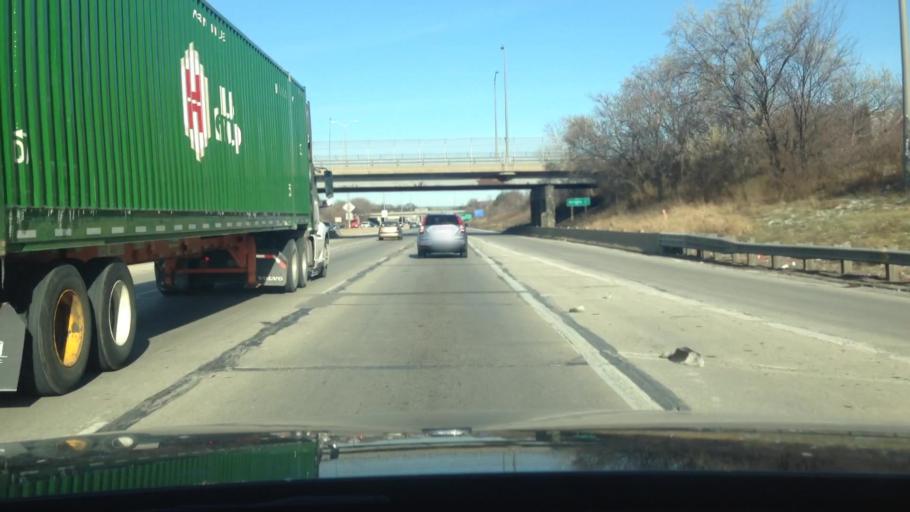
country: US
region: Wisconsin
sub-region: Milwaukee County
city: Milwaukee
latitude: 43.0632
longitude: -87.9205
